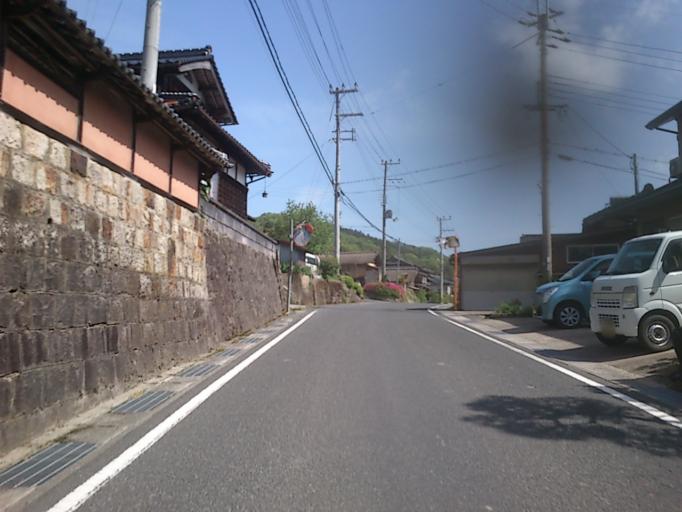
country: JP
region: Kyoto
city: Miyazu
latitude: 35.5627
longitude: 135.1131
